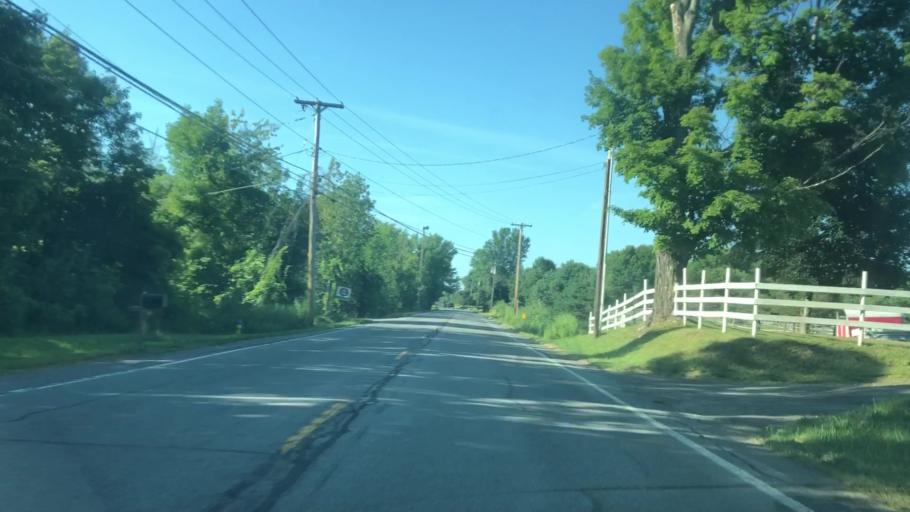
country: US
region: New York
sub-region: Wayne County
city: Ontario
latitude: 43.1567
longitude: -77.2916
